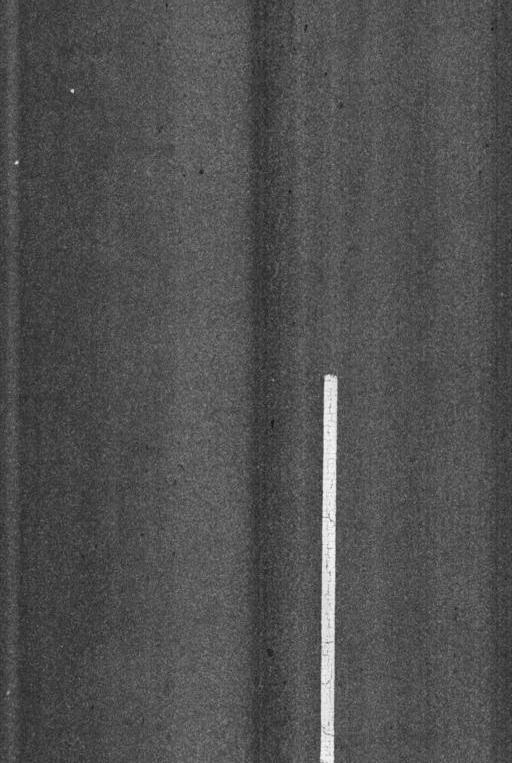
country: US
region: Washington, D.C.
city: Washington, D.C.
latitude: 38.8634
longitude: -77.0258
